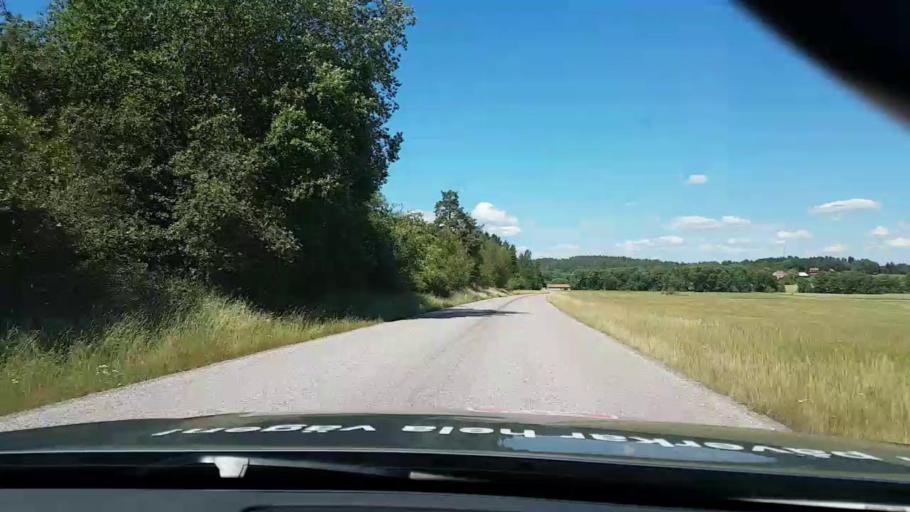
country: SE
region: Kalmar
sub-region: Vasterviks Kommun
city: Forserum
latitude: 57.9446
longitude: 16.4499
